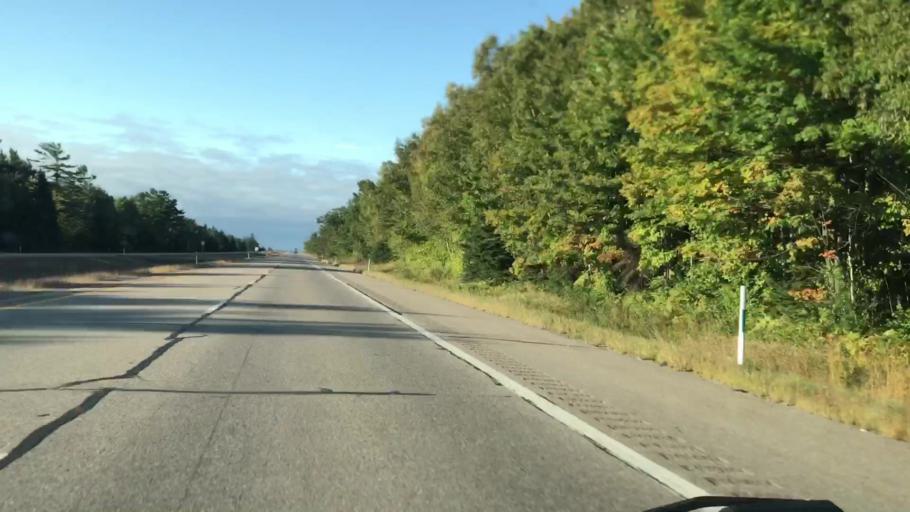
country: US
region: Michigan
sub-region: Chippewa County
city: Sault Ste. Marie
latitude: 46.4352
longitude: -84.3891
